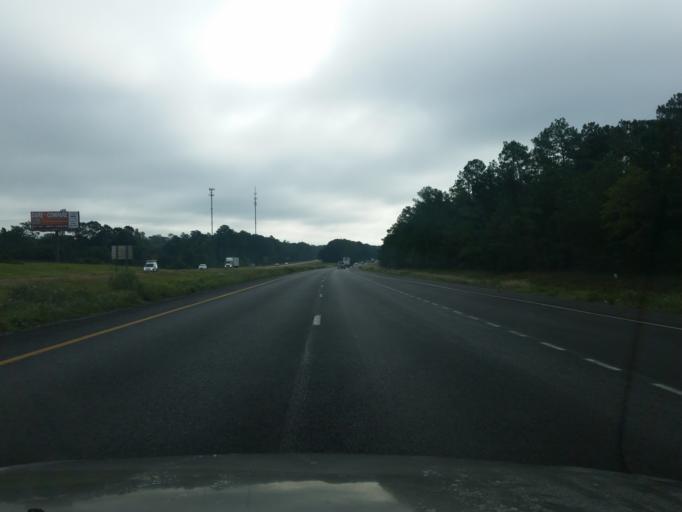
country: US
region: Alabama
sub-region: Baldwin County
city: Spanish Fort
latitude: 30.6629
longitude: -87.8464
